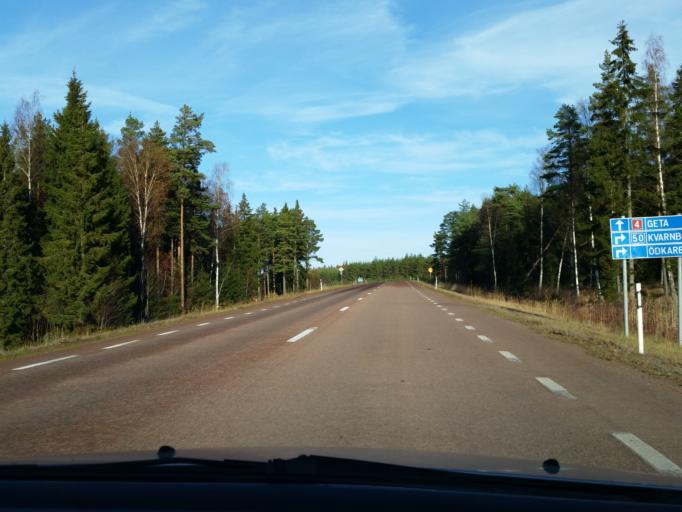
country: AX
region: Alands landsbygd
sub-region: Finstroem
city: Finstroem
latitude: 60.3020
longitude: 19.9525
